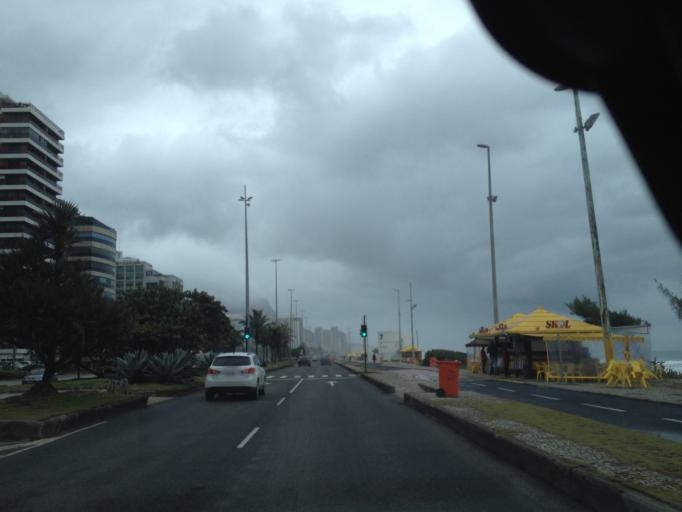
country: BR
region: Rio de Janeiro
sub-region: Rio De Janeiro
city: Rio de Janeiro
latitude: -23.0105
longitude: -43.3540
